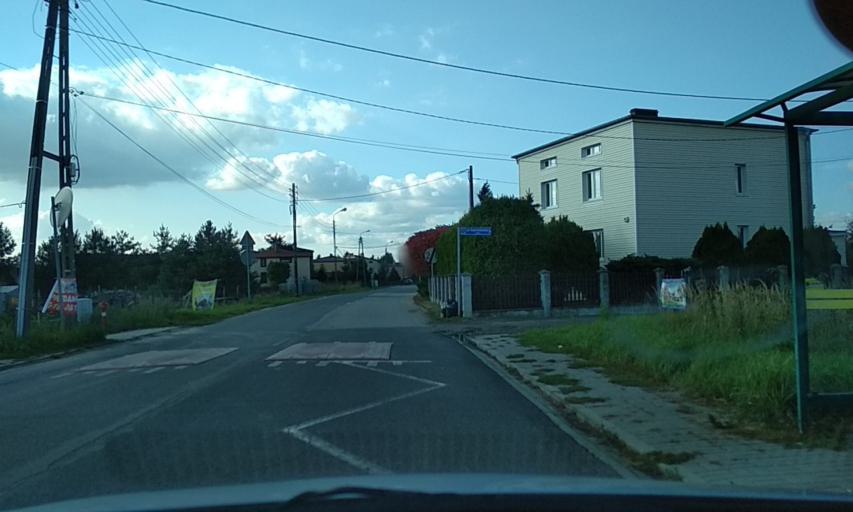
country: PL
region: Silesian Voivodeship
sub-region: Powiat bierunsko-ledzinski
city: Ledziny
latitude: 50.1717
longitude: 19.1466
